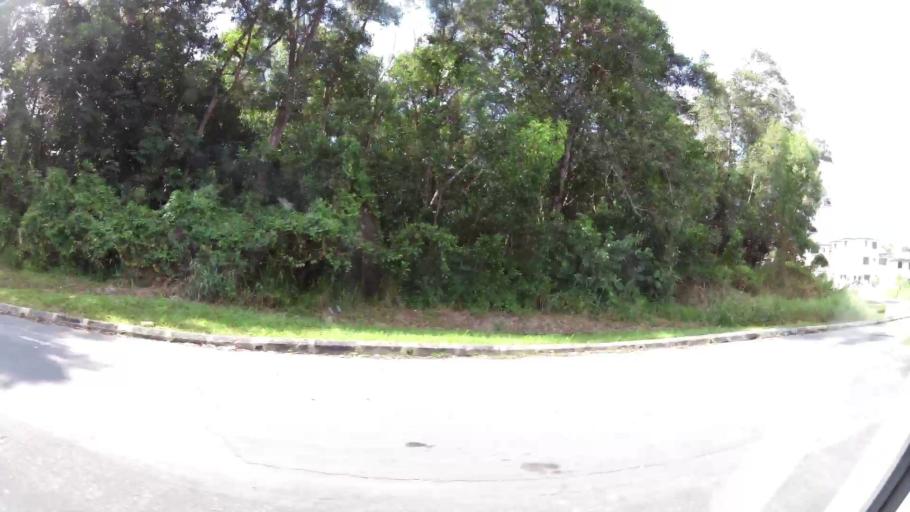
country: BN
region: Brunei and Muara
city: Bandar Seri Begawan
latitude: 4.9514
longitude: 114.9460
